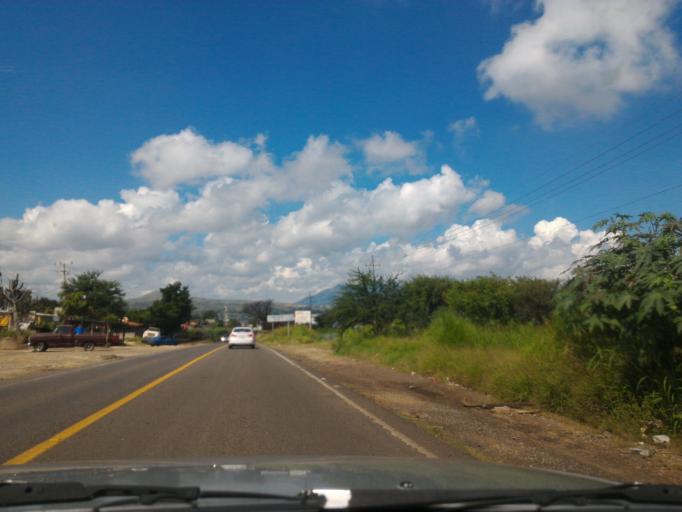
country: MX
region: Jalisco
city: Tequila
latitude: 20.8768
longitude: -103.8131
